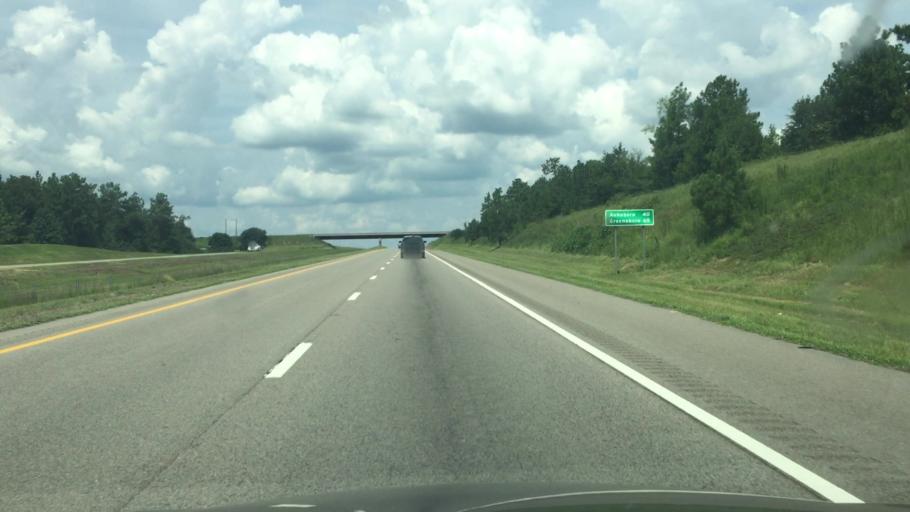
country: US
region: North Carolina
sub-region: Richmond County
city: Ellerbe
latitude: 35.1840
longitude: -79.7181
